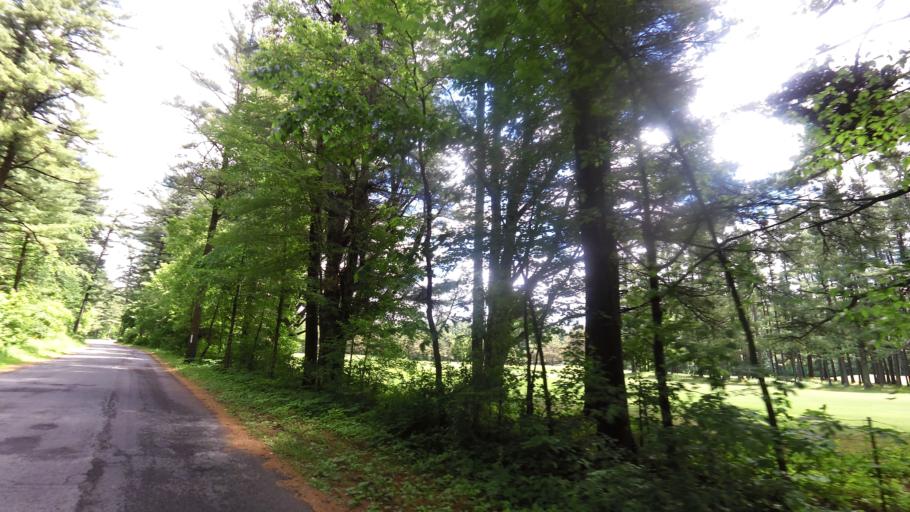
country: CA
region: Quebec
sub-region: Laurentides
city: Oka
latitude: 45.4685
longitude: -74.0932
